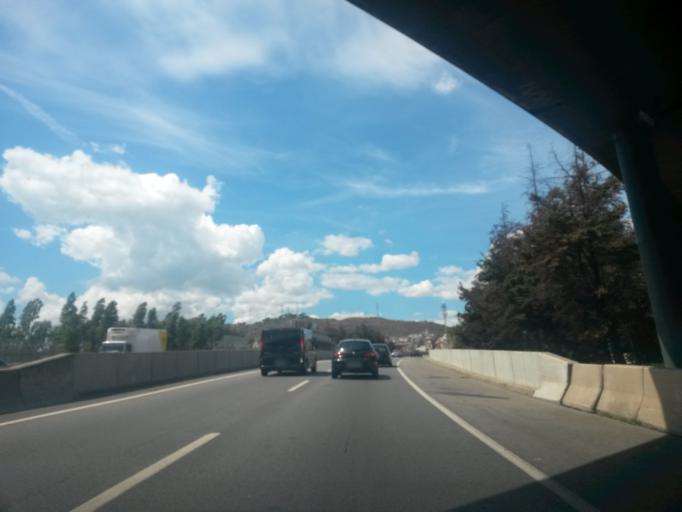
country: ES
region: Catalonia
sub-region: Provincia de Barcelona
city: Santa Coloma de Gramenet
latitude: 41.4496
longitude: 2.1980
